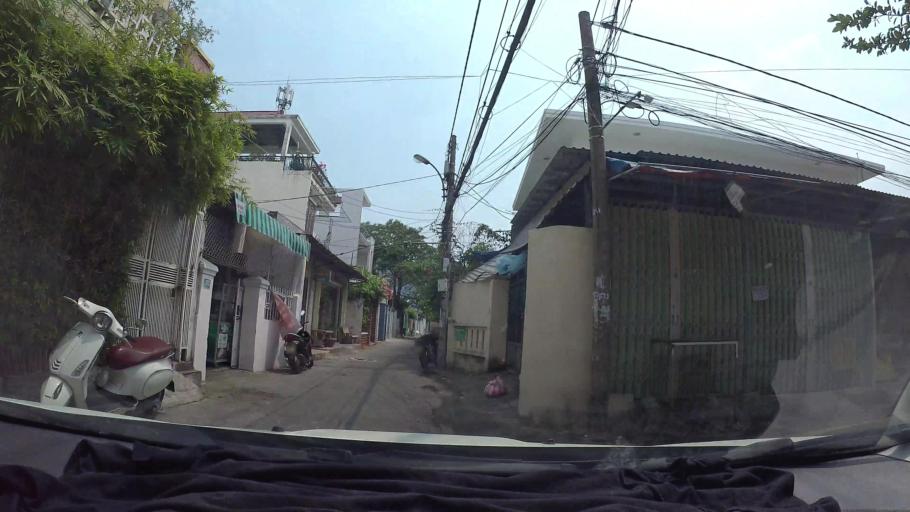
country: VN
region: Da Nang
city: Da Nang
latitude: 16.0824
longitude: 108.2178
